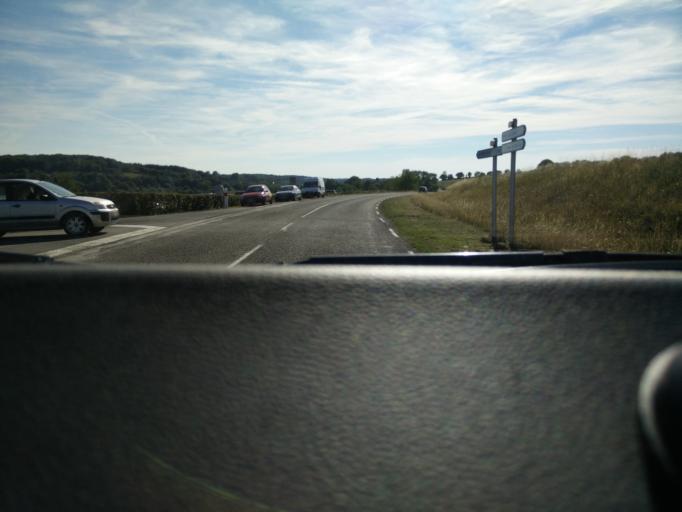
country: FR
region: Nord-Pas-de-Calais
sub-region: Departement du Nord
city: Trelon
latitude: 50.1228
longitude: 4.1236
